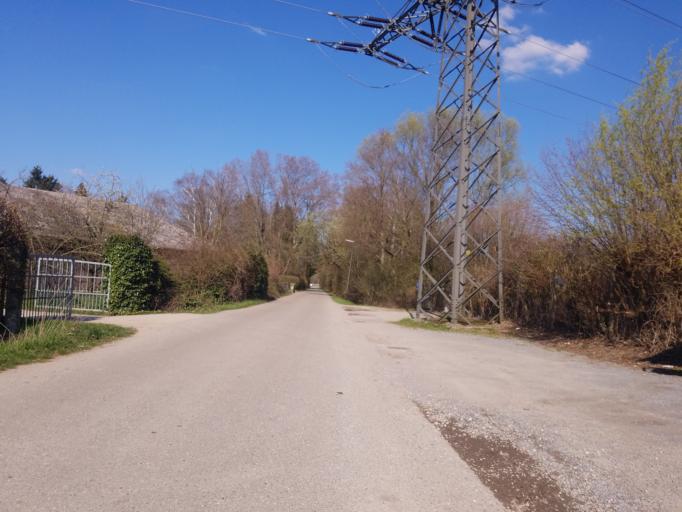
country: DE
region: Baden-Wuerttemberg
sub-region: Karlsruhe Region
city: Schwarzach
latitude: 48.7487
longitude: 8.0613
